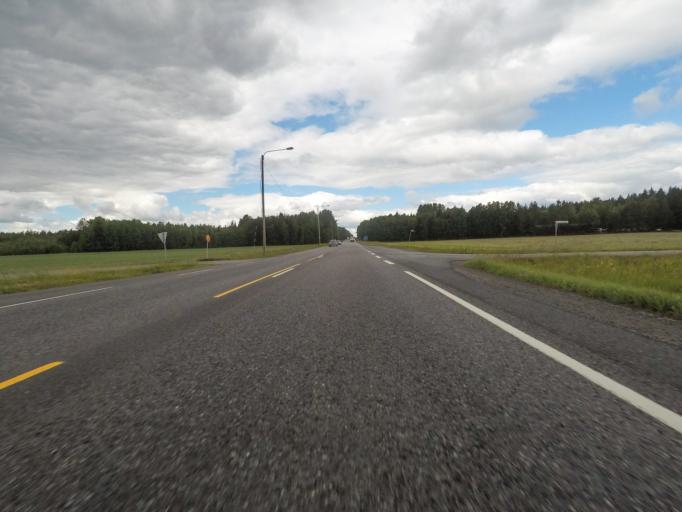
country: FI
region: Varsinais-Suomi
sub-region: Turku
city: Piikkioe
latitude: 60.4449
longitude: 22.4810
